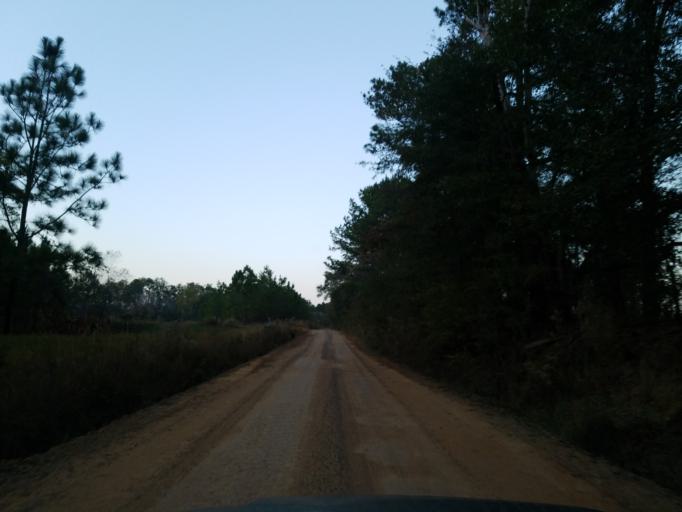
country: US
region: Georgia
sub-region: Turner County
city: Ashburn
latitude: 31.7312
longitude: -83.4836
